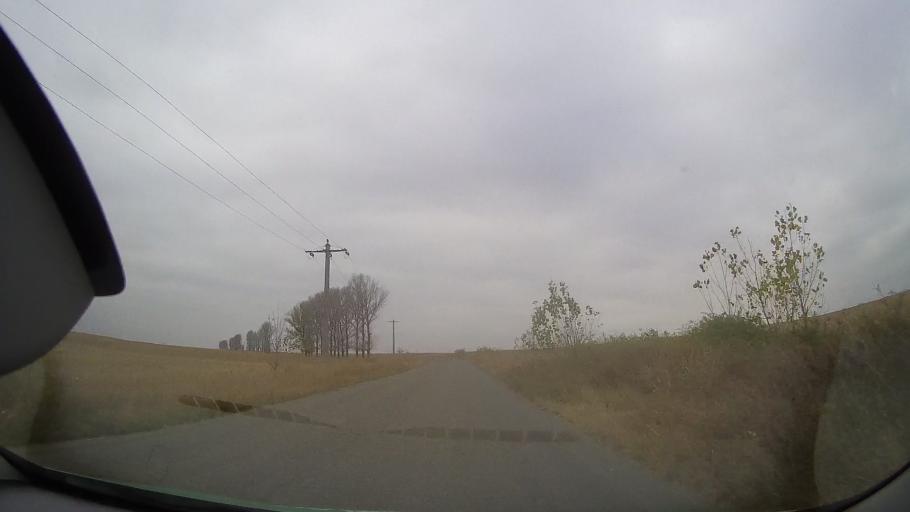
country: RO
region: Buzau
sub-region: Comuna Pogoanele
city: Pogoanele
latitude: 44.9661
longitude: 27.0241
